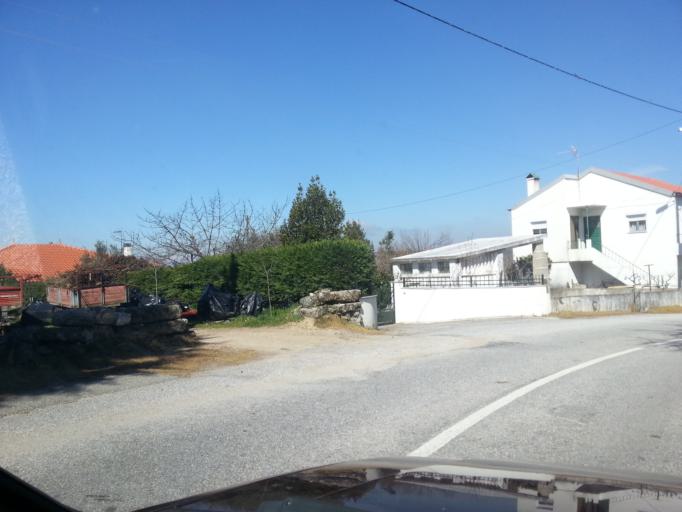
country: PT
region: Guarda
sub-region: Fornos de Algodres
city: Fornos de Algodres
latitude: 40.6563
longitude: -7.5342
